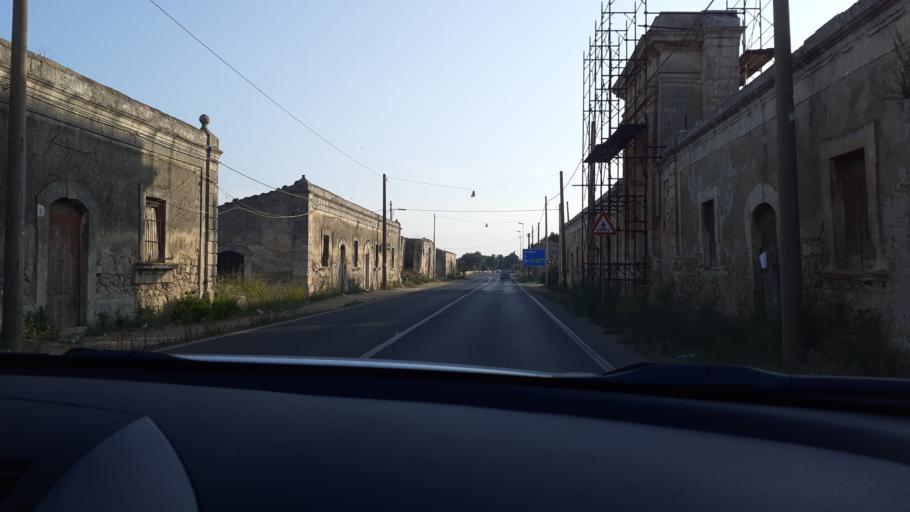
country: IT
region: Sicily
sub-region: Provincia di Siracusa
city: Cassibile
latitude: 36.9733
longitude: 15.1935
